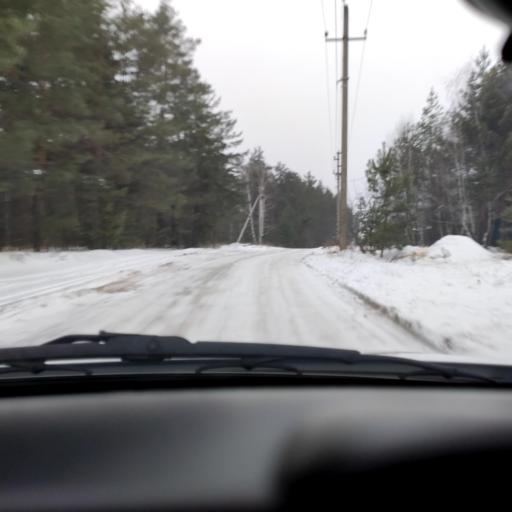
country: RU
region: Voronezj
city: Ramon'
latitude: 51.8855
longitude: 39.2567
